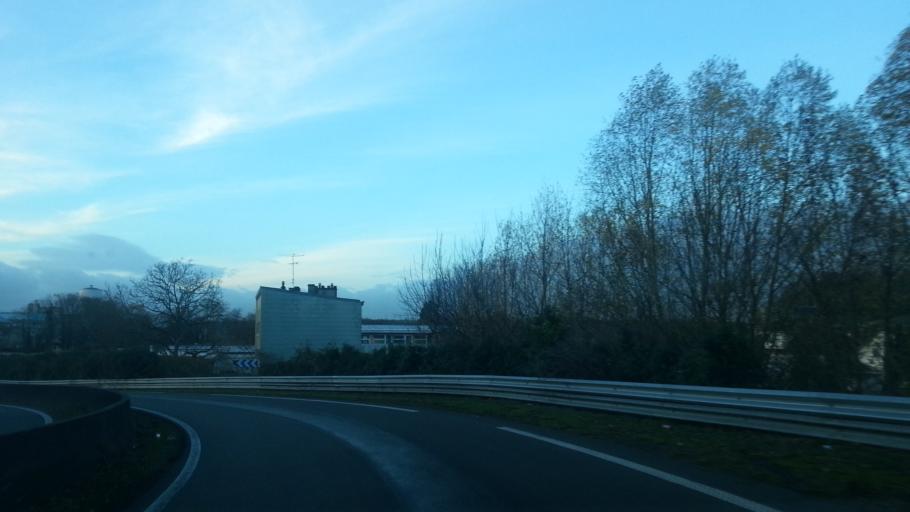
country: FR
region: Picardie
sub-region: Departement de l'Oise
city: Montataire
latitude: 49.2569
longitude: 2.4500
